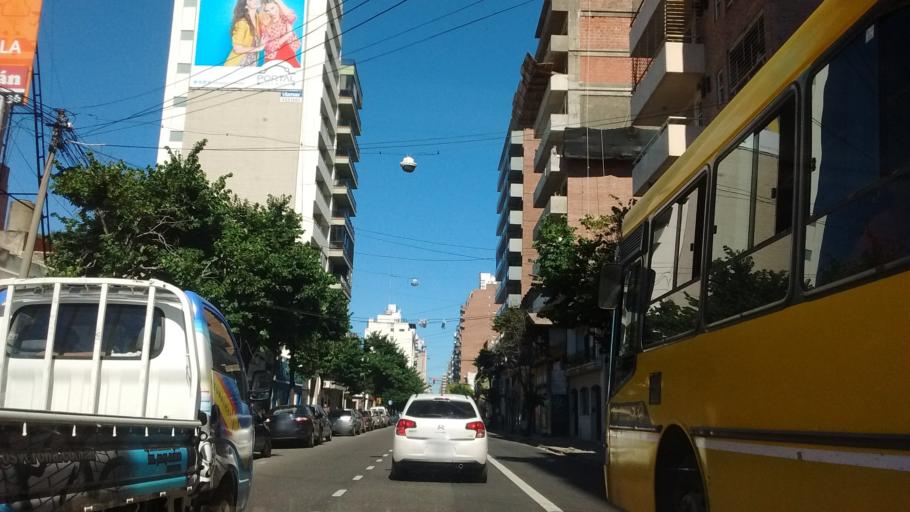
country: AR
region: Santa Fe
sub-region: Departamento de Rosario
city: Rosario
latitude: -32.9423
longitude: -60.6613
